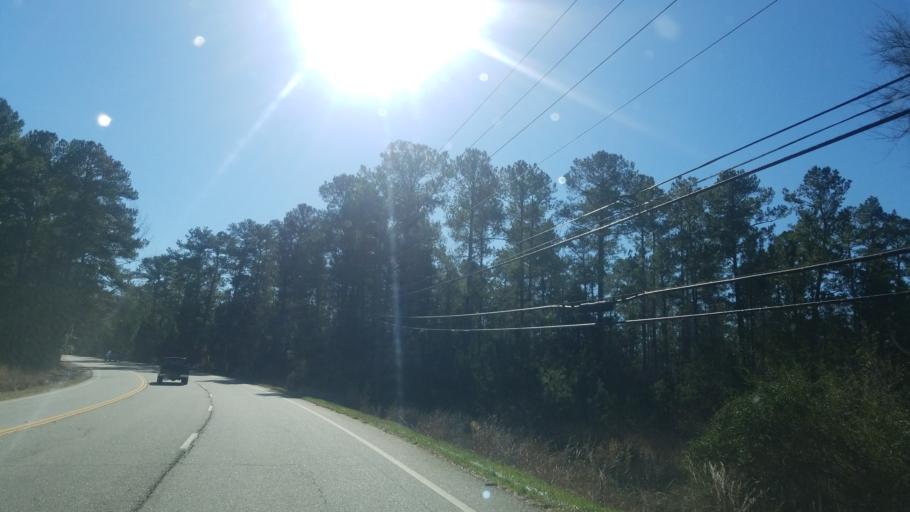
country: US
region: Alabama
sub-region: Russell County
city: Phenix City
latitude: 32.5604
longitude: -85.0104
